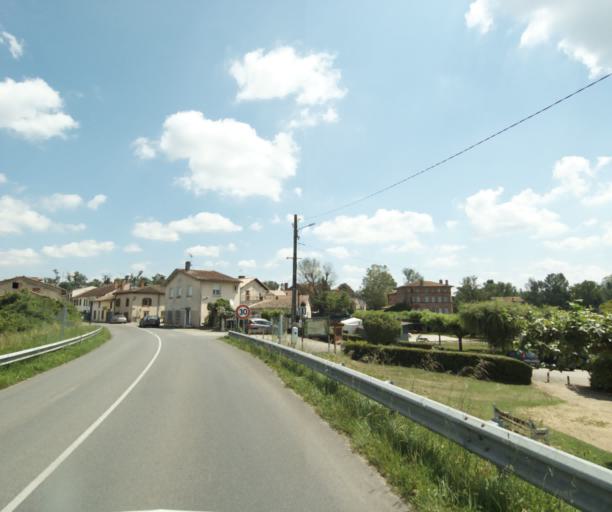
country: FR
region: Midi-Pyrenees
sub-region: Departement du Tarn-et-Garonne
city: Montauban
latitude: 44.0741
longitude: 1.3696
